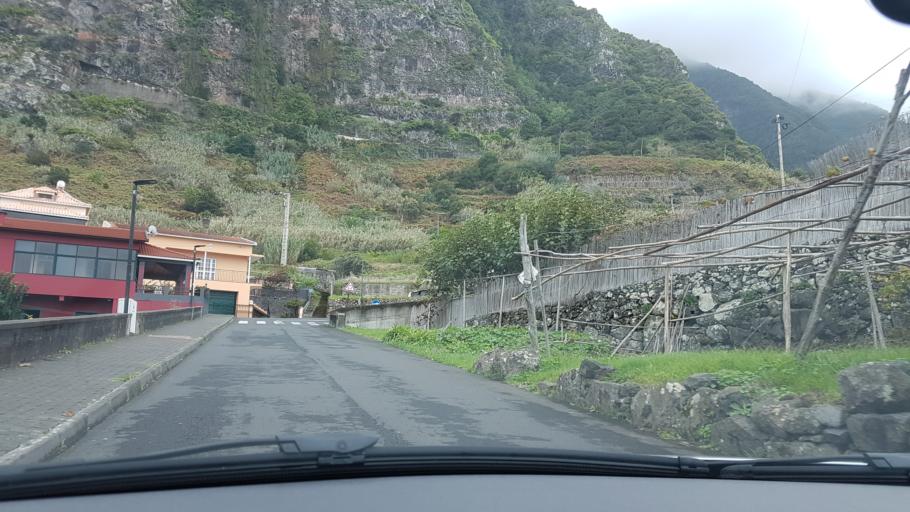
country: PT
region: Madeira
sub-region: Sao Vicente
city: Sao Vicente
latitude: 32.8272
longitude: -16.9851
